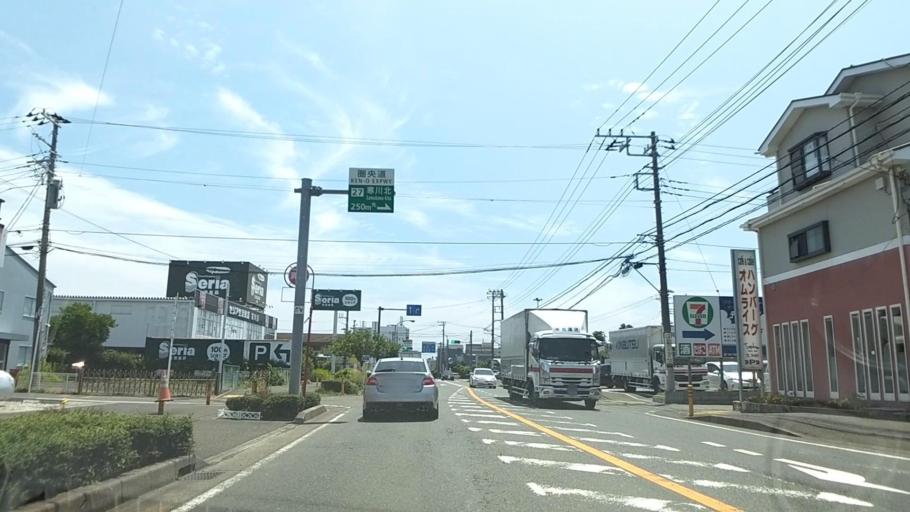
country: JP
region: Kanagawa
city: Atsugi
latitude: 35.3916
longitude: 139.3802
